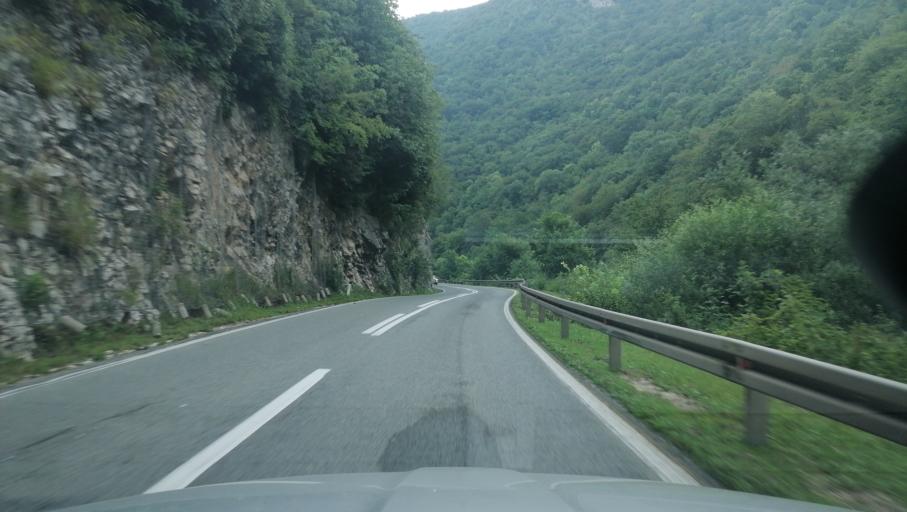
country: BA
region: Republika Srpska
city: Mrkonjic Grad
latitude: 44.5841
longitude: 17.1339
